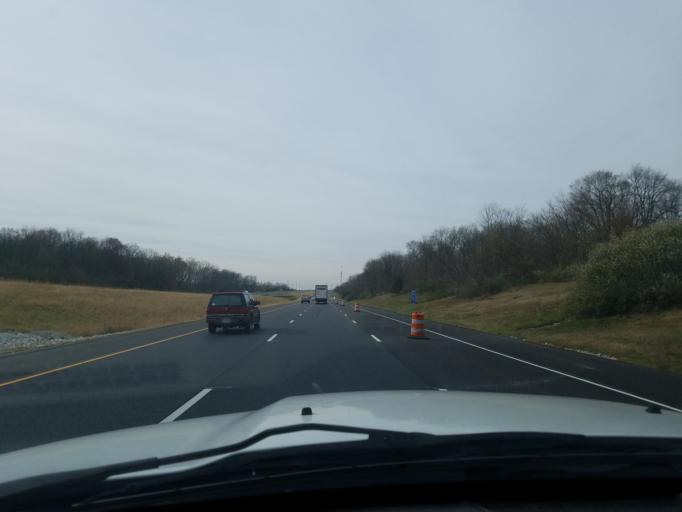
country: US
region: Indiana
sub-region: Hancock County
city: Fortville
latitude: 39.9914
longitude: -85.8977
